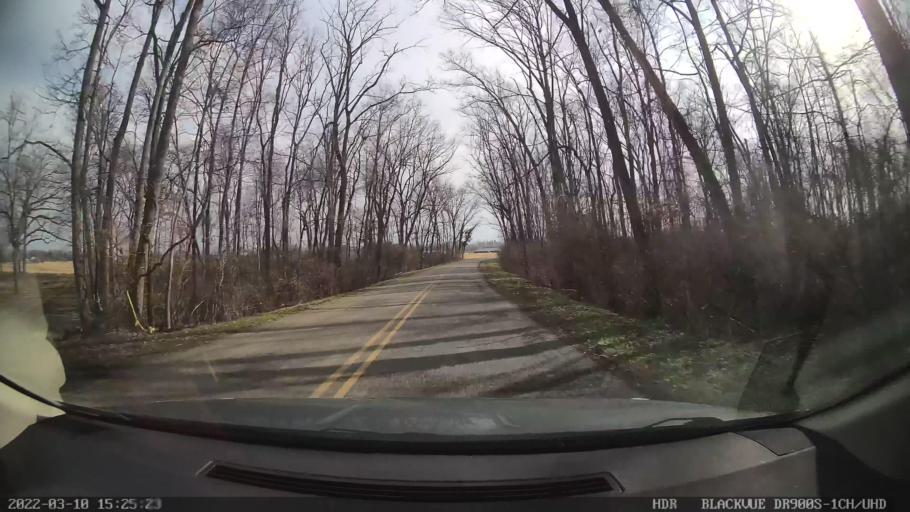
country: US
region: Pennsylvania
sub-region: Berks County
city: Oley
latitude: 40.3553
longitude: -75.7876
